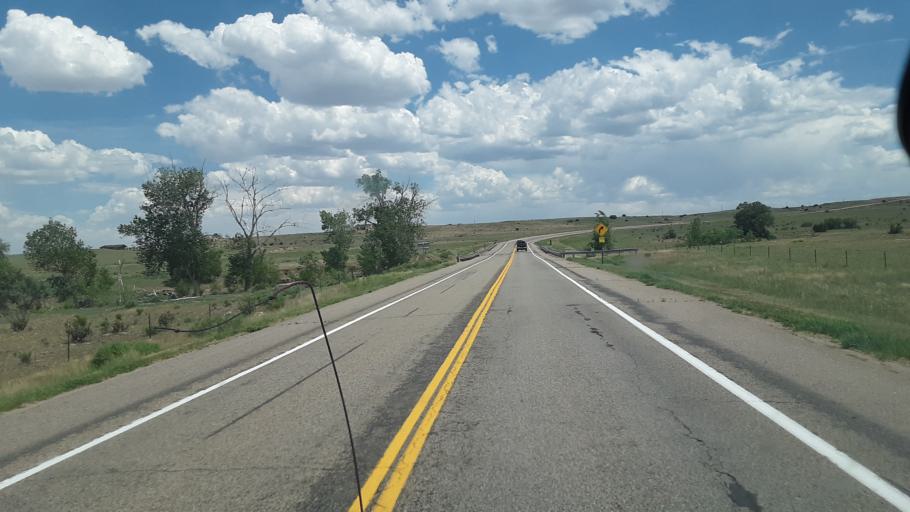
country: US
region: Colorado
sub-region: Fremont County
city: Florence
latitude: 38.3012
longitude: -105.0921
